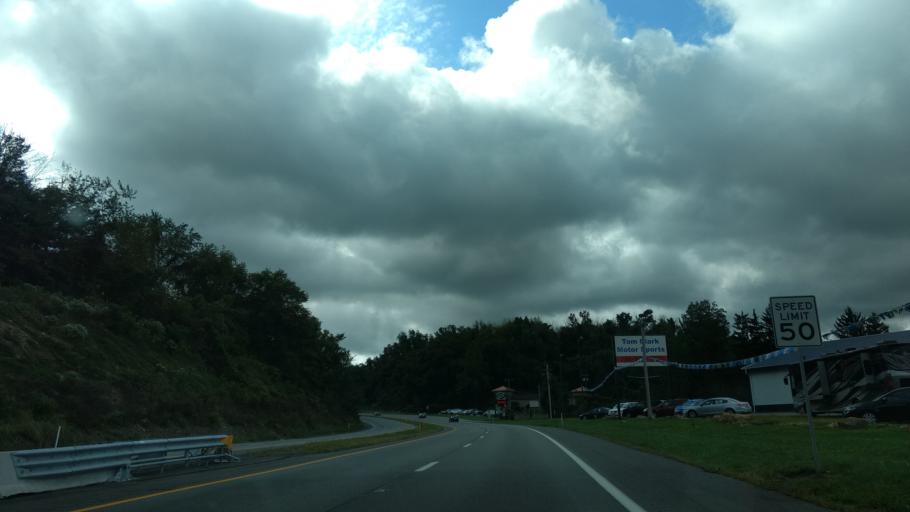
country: US
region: Pennsylvania
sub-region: Westmoreland County
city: Fellsburg
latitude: 40.1774
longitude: -79.8038
